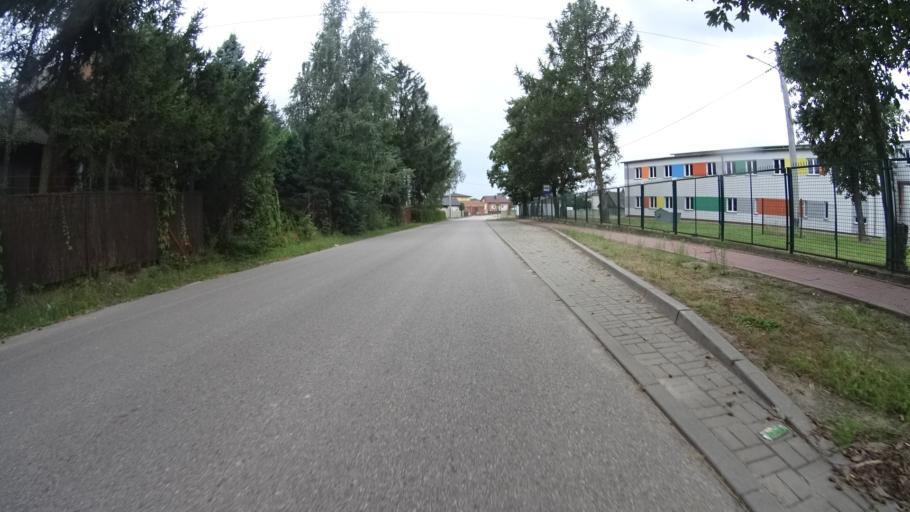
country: PL
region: Masovian Voivodeship
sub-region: Powiat bialobrzeski
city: Wysmierzyce
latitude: 51.6656
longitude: 20.8555
